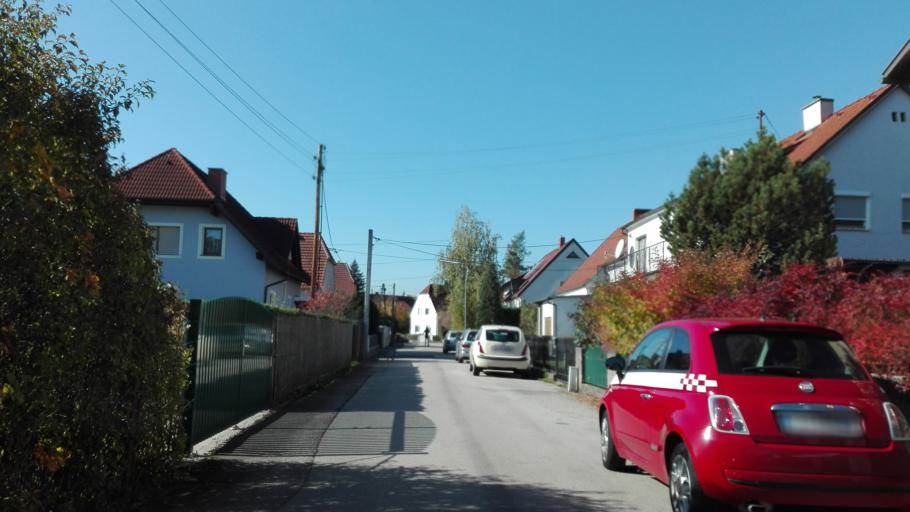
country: AT
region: Upper Austria
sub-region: Politischer Bezirk Linz-Land
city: Leonding
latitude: 48.2517
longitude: 14.2642
